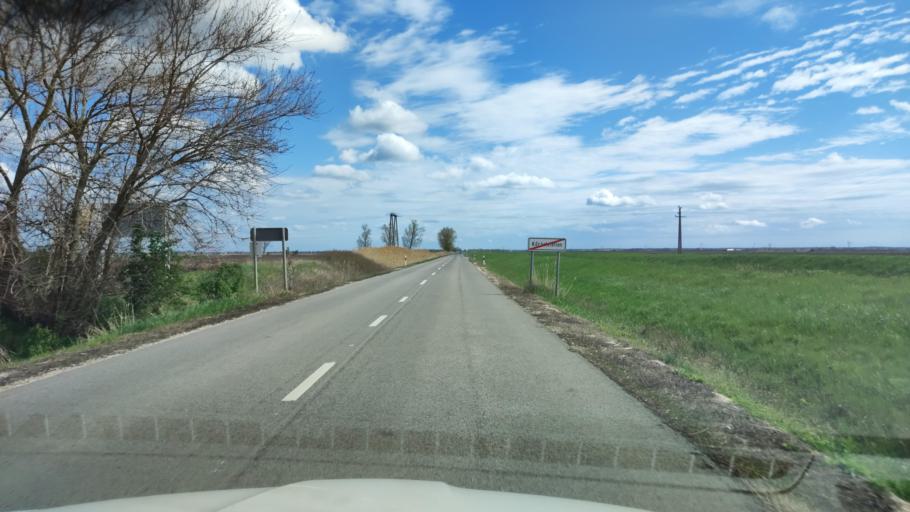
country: HU
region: Pest
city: Jaszkarajeno
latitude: 47.1011
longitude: 20.0286
